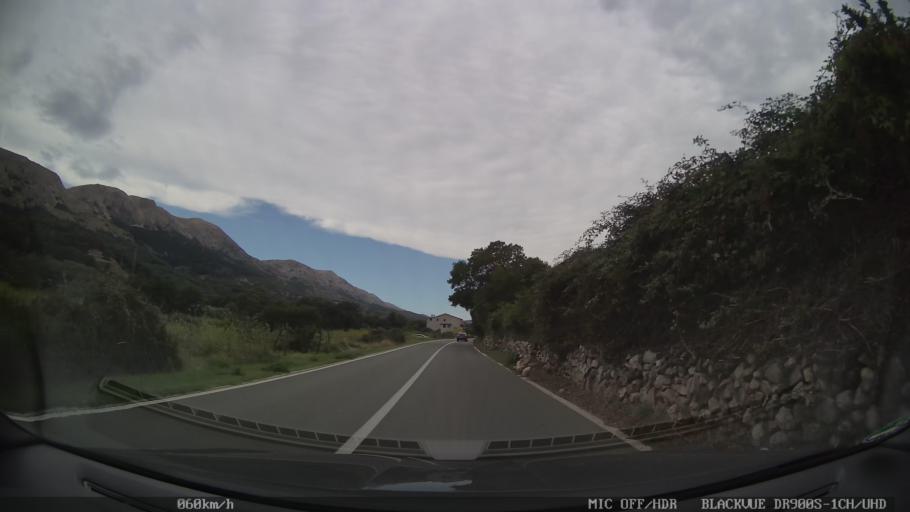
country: HR
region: Primorsko-Goranska
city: Punat
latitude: 44.9862
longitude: 14.7208
